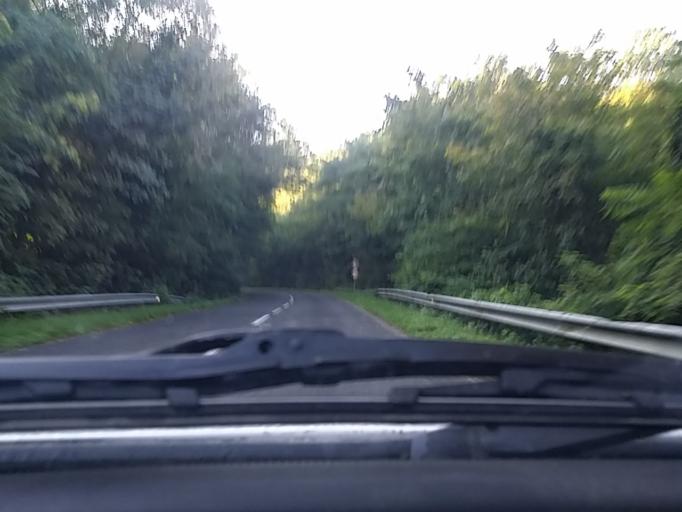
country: HU
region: Pest
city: Visegrad
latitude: 47.7648
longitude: 18.9540
